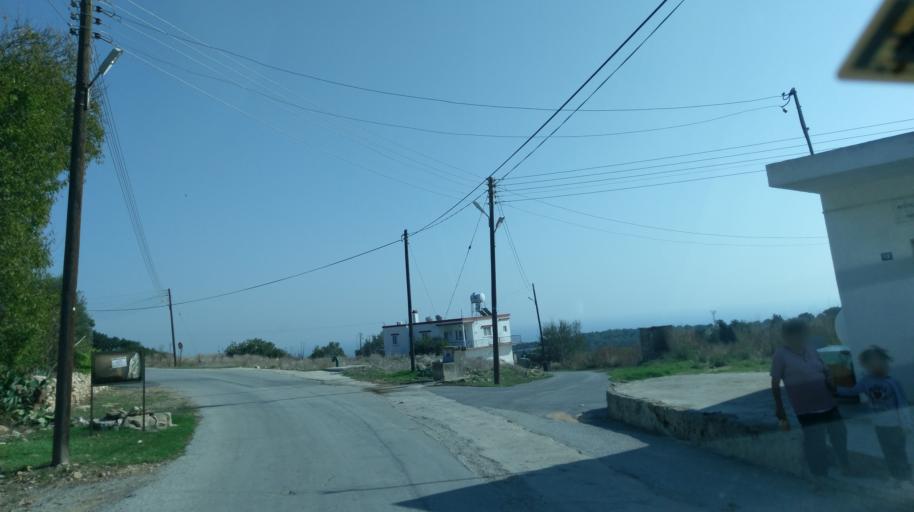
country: CY
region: Ammochostos
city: Leonarisso
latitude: 35.4905
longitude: 34.2192
